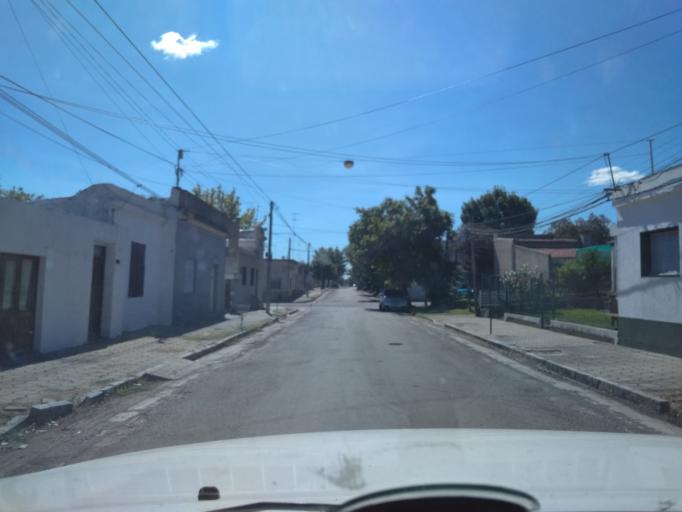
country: UY
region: Florida
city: Florida
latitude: -34.1033
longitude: -56.2189
